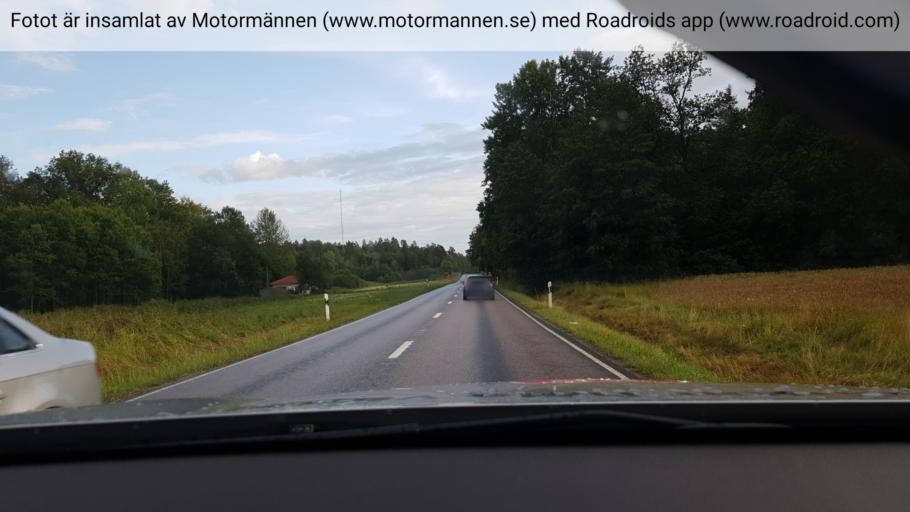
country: SE
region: Stockholm
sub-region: Norrtalje Kommun
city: Norrtalje
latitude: 59.8103
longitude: 18.6493
